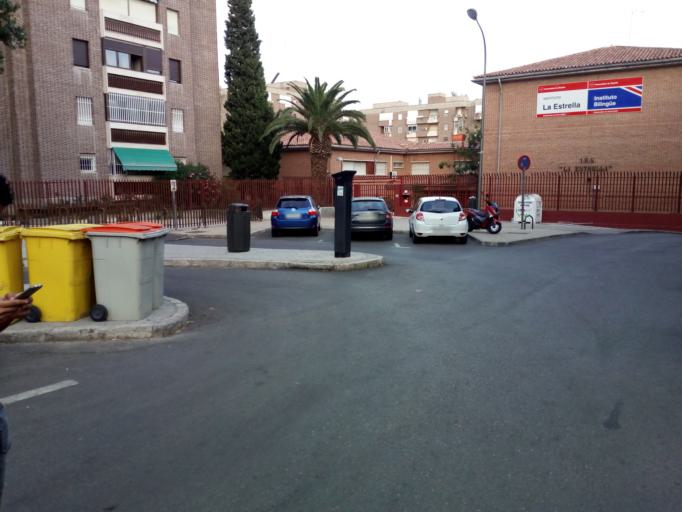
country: ES
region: Madrid
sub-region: Provincia de Madrid
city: Retiro
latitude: 40.4095
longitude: -3.6670
